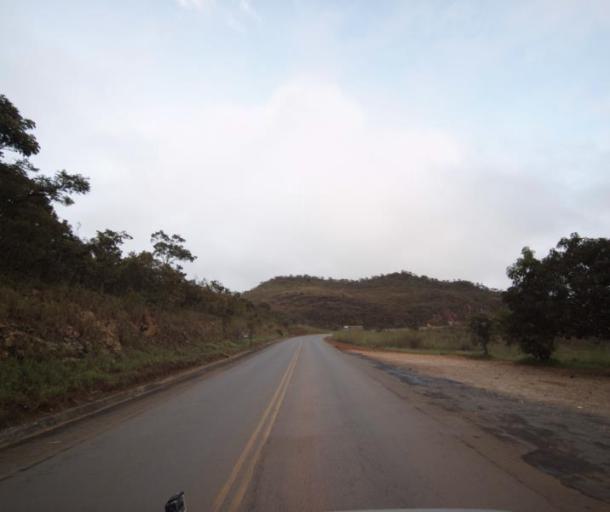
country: BR
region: Goias
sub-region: Pirenopolis
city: Pirenopolis
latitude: -15.8479
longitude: -48.7676
